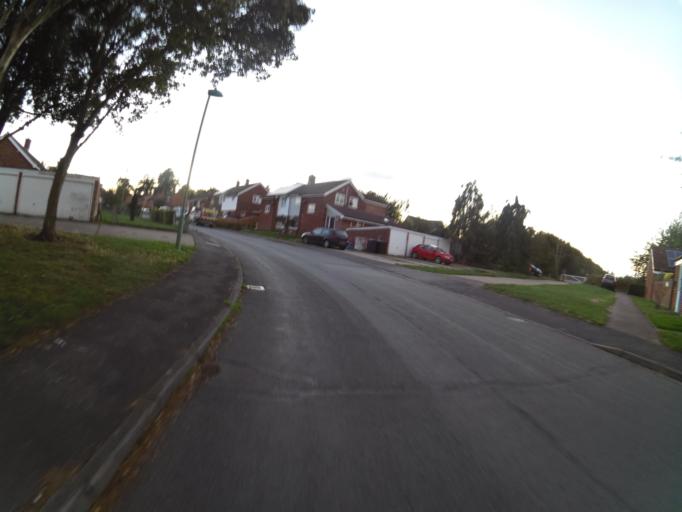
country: GB
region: England
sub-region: Suffolk
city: Bramford
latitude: 52.0802
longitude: 1.0975
